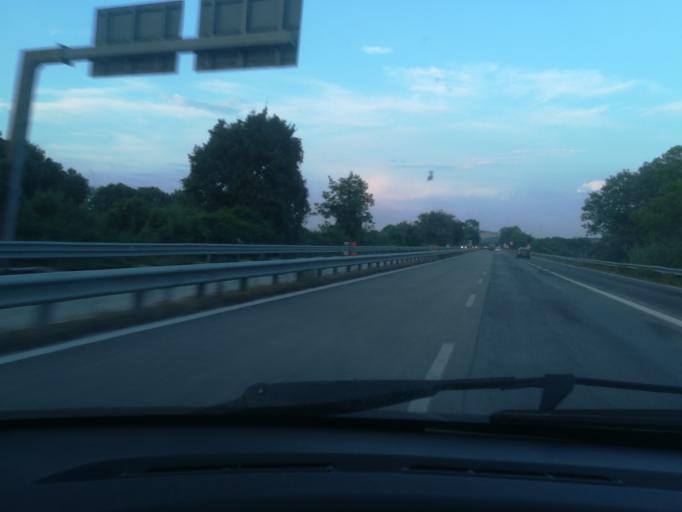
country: IT
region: The Marches
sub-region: Provincia di Macerata
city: Casette Verdini
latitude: 43.2343
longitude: 13.3720
